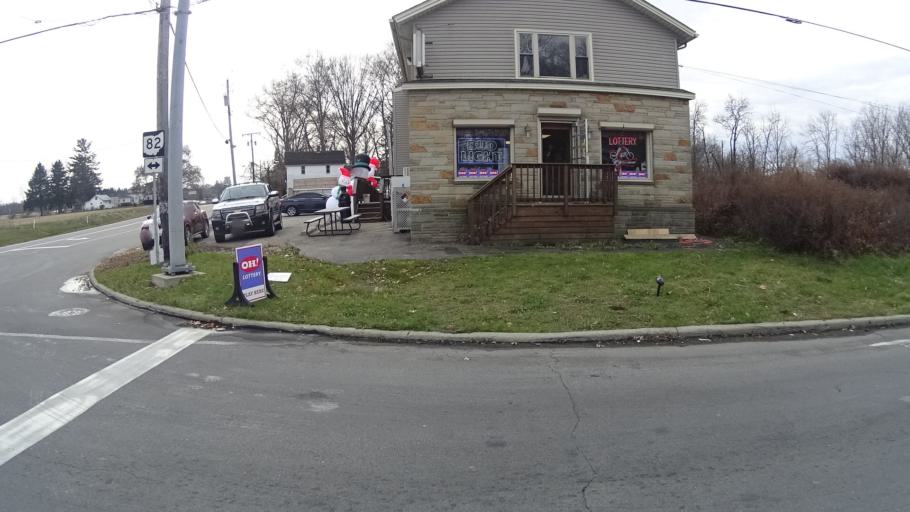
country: US
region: Ohio
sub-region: Cuyahoga County
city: Olmsted Falls
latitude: 41.3126
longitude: -81.9156
